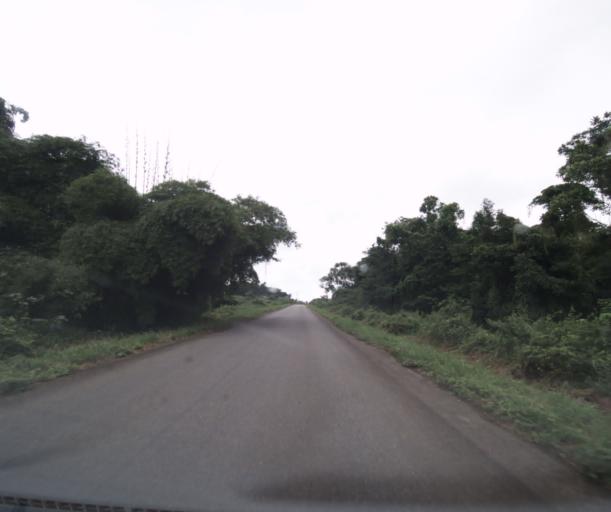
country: CM
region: Littoral
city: Edea
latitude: 3.7183
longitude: 10.1075
